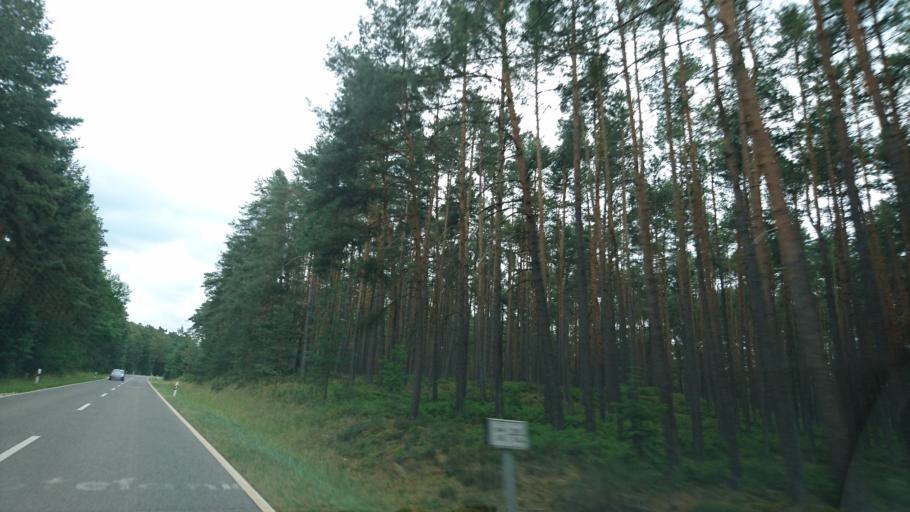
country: DE
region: Bavaria
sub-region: Regierungsbezirk Mittelfranken
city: Heideck
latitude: 49.1779
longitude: 11.1153
